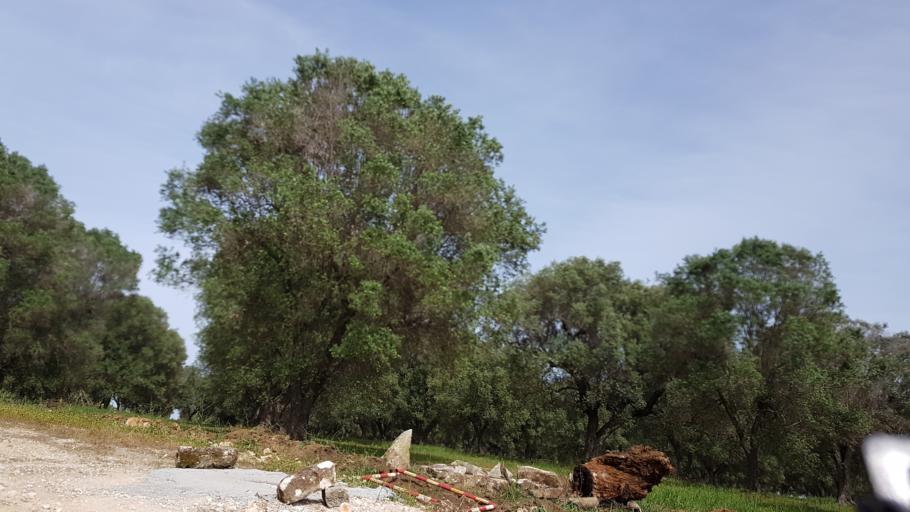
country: IT
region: Apulia
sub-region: Provincia di Brindisi
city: La Rosa
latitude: 40.5891
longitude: 18.0020
